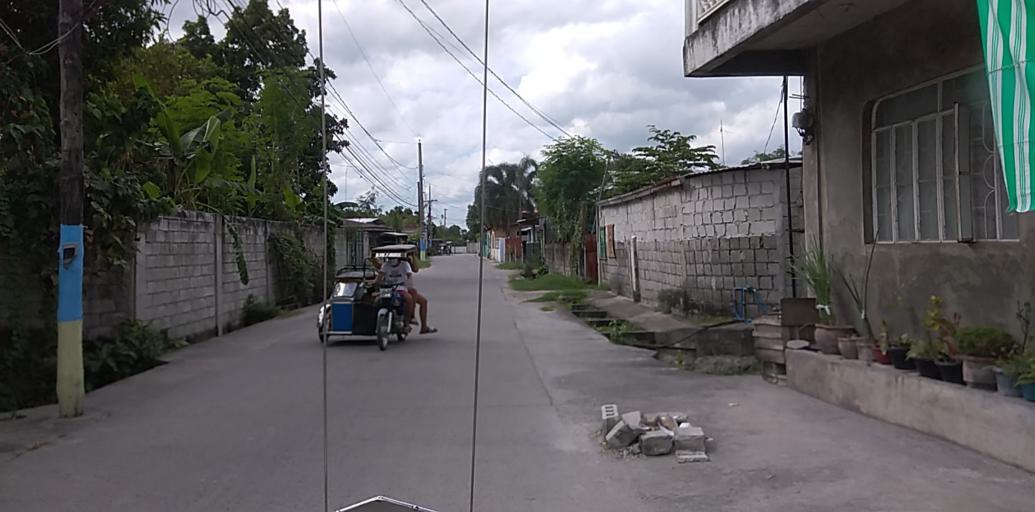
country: PH
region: Central Luzon
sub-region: Province of Pampanga
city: Porac
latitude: 15.0700
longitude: 120.5422
